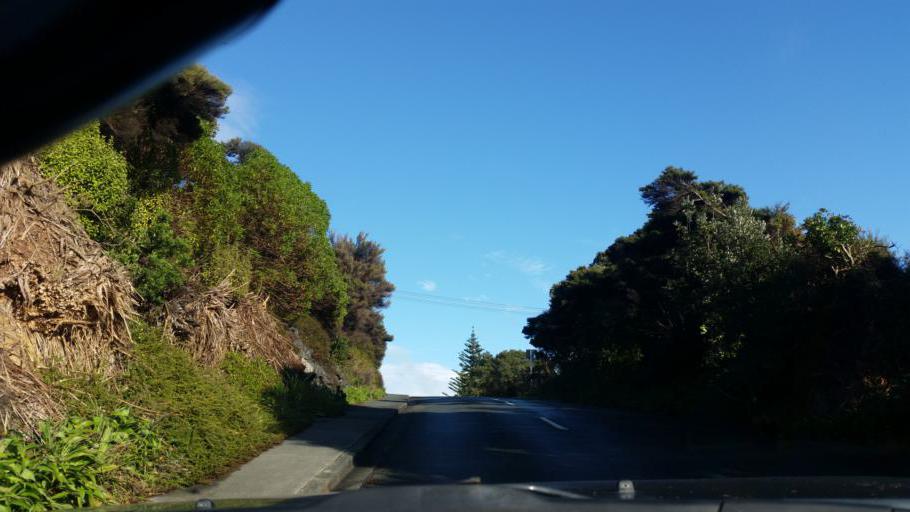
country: NZ
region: Auckland
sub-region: Auckland
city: Wellsford
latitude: -36.0903
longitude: 174.5894
